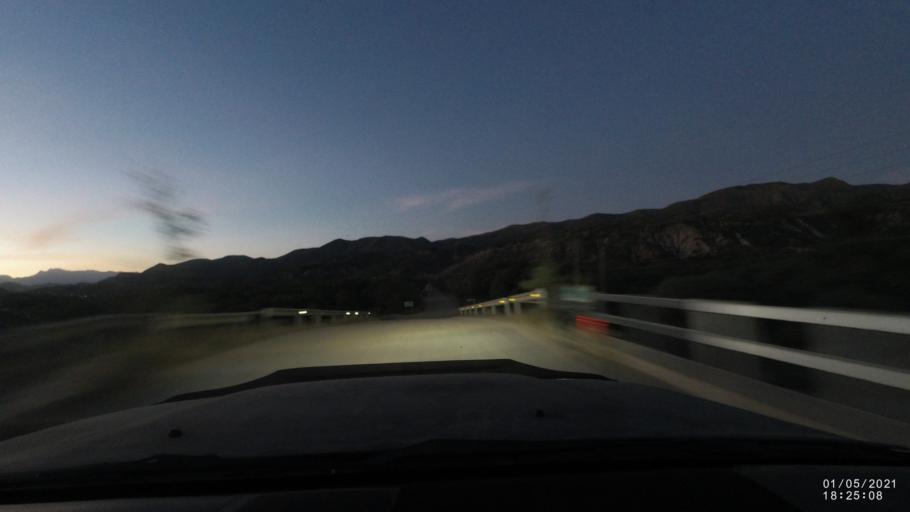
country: BO
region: Cochabamba
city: Capinota
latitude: -17.6571
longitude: -66.2429
